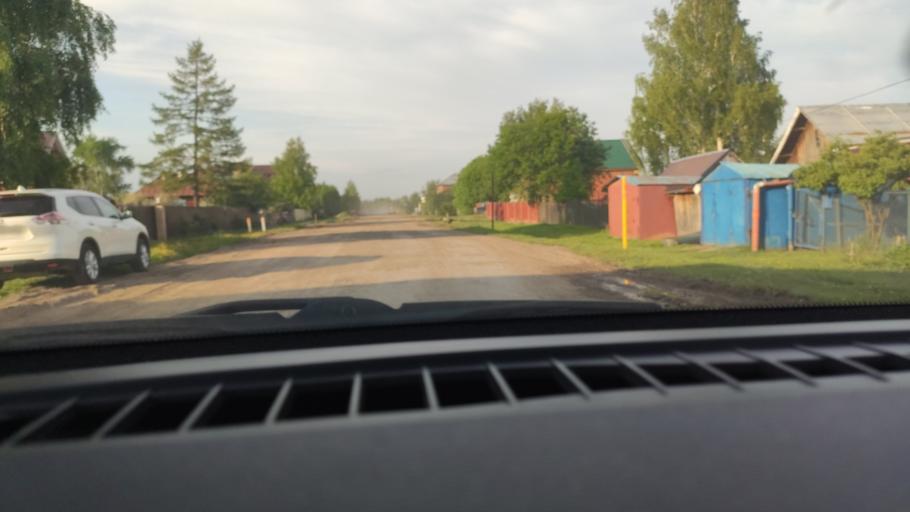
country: RU
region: Perm
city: Kultayevo
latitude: 57.9278
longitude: 56.0120
